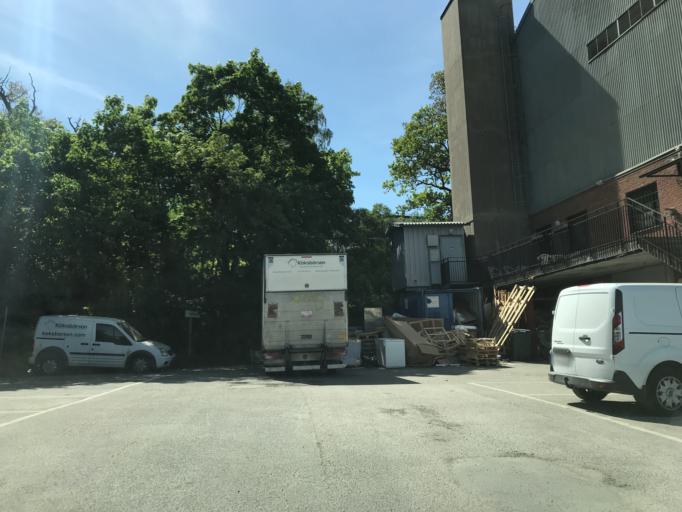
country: SE
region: Stockholm
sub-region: Stockholms Kommun
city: OEstermalm
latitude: 59.3514
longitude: 18.0878
